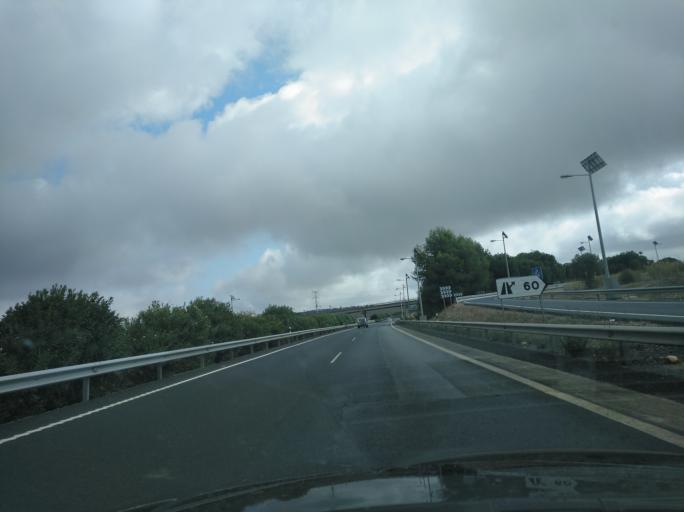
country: ES
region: Andalusia
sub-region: Provincia de Huelva
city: Bonares
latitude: 37.3427
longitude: -6.6791
